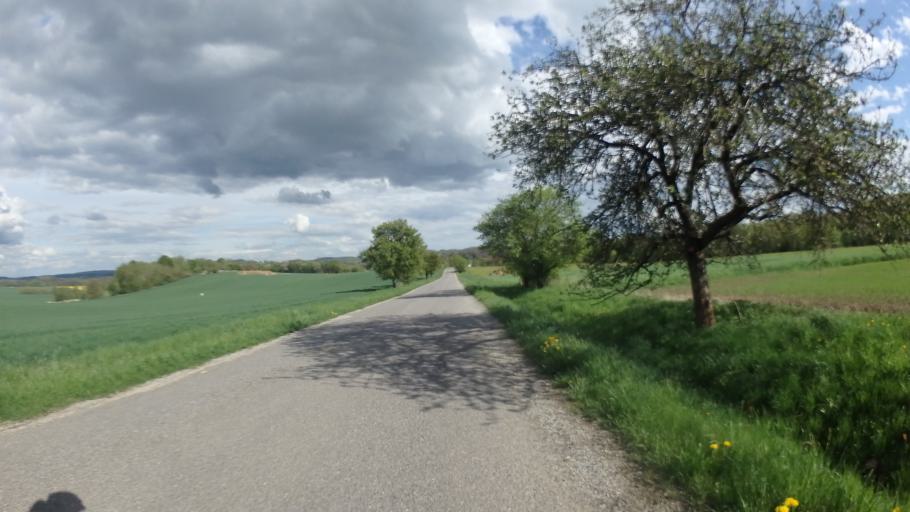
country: CZ
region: Vysocina
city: Merin
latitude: 49.3419
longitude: 15.8911
